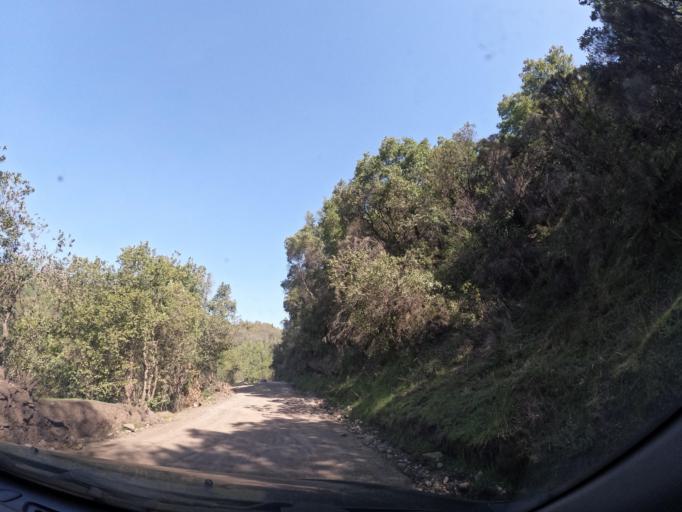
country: CL
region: Maule
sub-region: Provincia de Linares
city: Longavi
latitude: -36.2404
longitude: -71.4406
